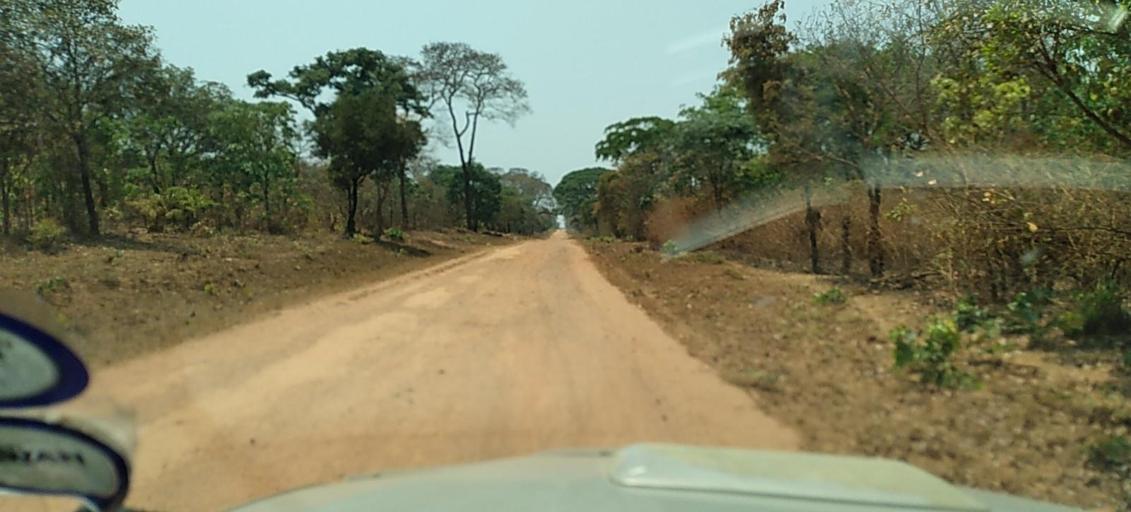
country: ZM
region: North-Western
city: Kasempa
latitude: -13.5504
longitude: 26.0280
